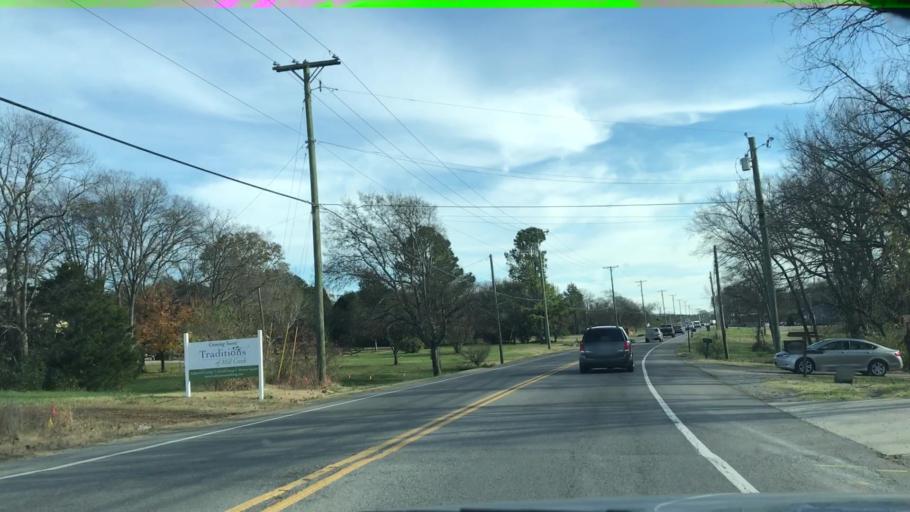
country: US
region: Tennessee
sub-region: Williamson County
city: Nolensville
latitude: 35.9946
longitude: -86.6867
